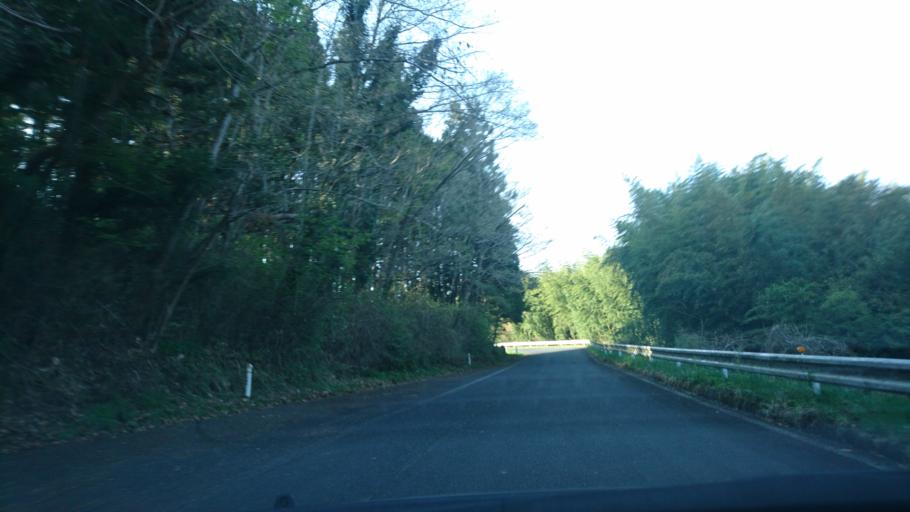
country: JP
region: Iwate
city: Ichinoseki
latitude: 38.8928
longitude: 141.2902
